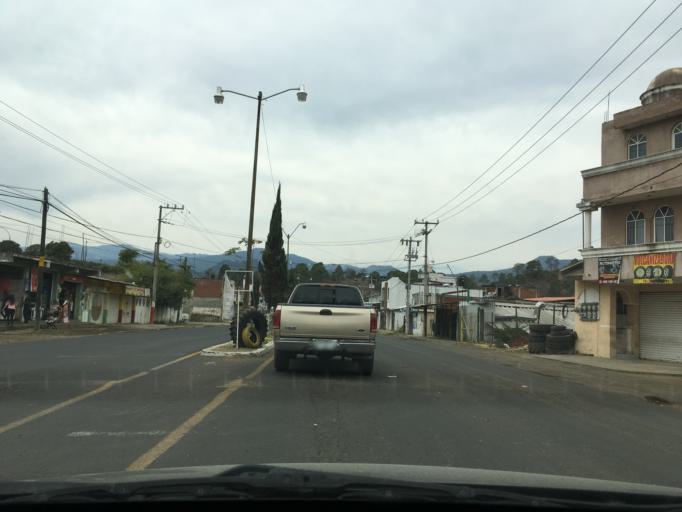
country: MX
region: Michoacan
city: Nuevo San Juan Parangaricutiro
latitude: 19.4129
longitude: -102.1168
